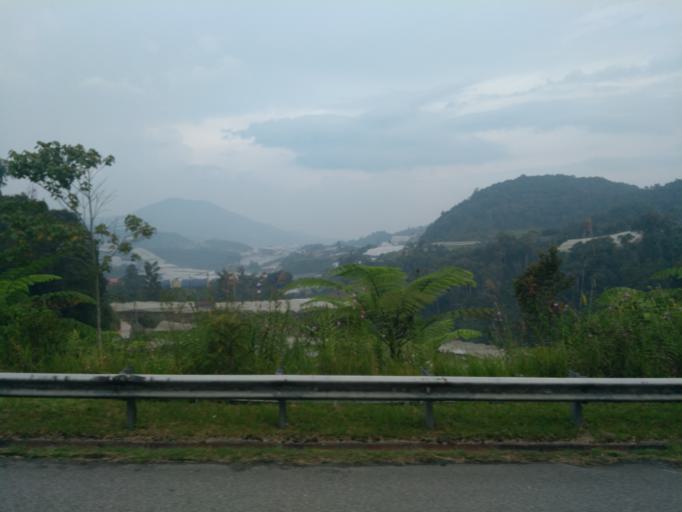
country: MY
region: Pahang
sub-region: Cameron Highlands
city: Tanah Rata
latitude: 4.5781
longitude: 101.3842
